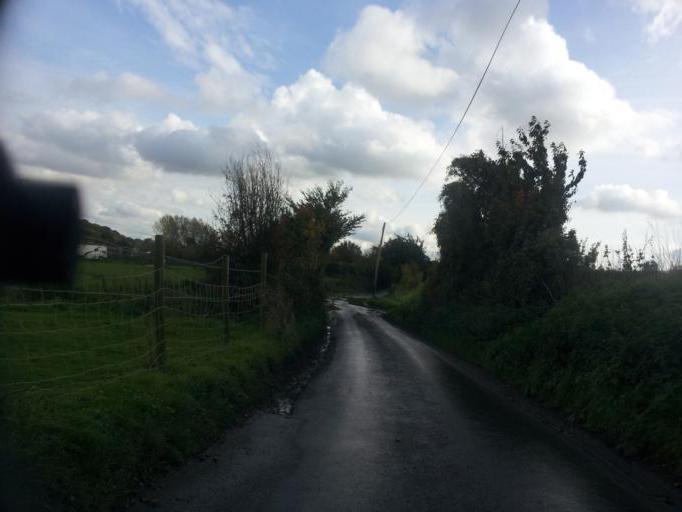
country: GB
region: England
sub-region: Kent
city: Newington
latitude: 51.3617
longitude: 0.6631
